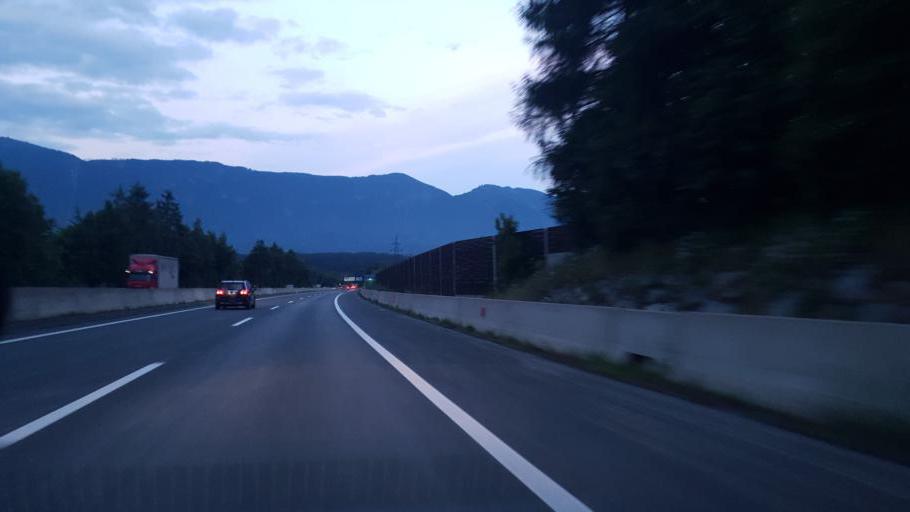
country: AT
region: Carinthia
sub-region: Politischer Bezirk Spittal an der Drau
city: Seeboden
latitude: 46.8377
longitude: 13.4942
